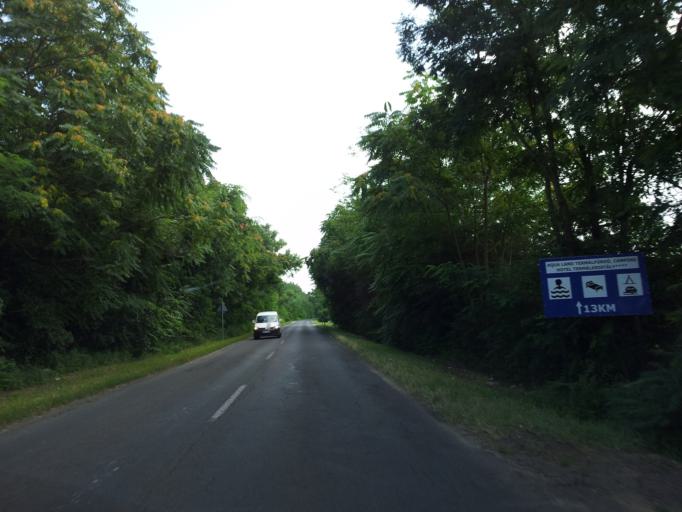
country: HU
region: Pest
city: Szigetcsep
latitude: 47.2947
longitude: 18.9804
